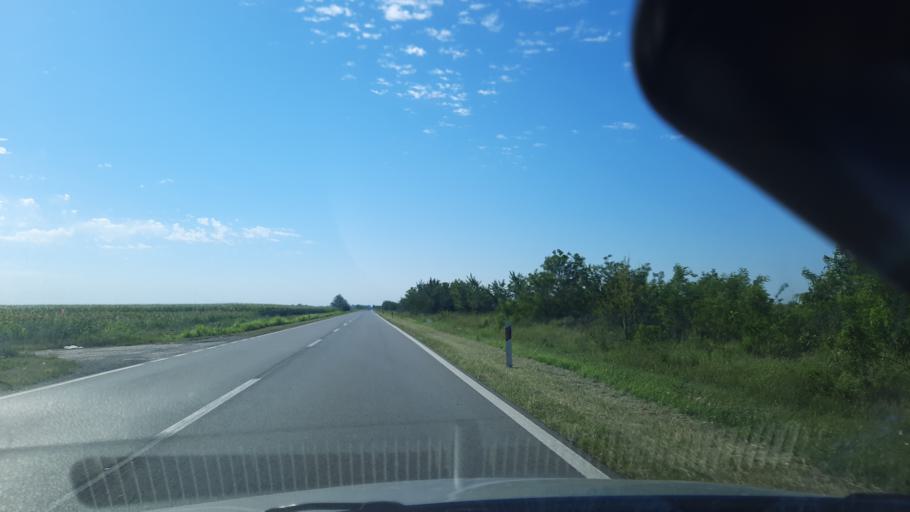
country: RS
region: Autonomna Pokrajina Vojvodina
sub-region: Juznobanatski Okrug
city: Kovin
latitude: 44.7813
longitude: 20.9297
